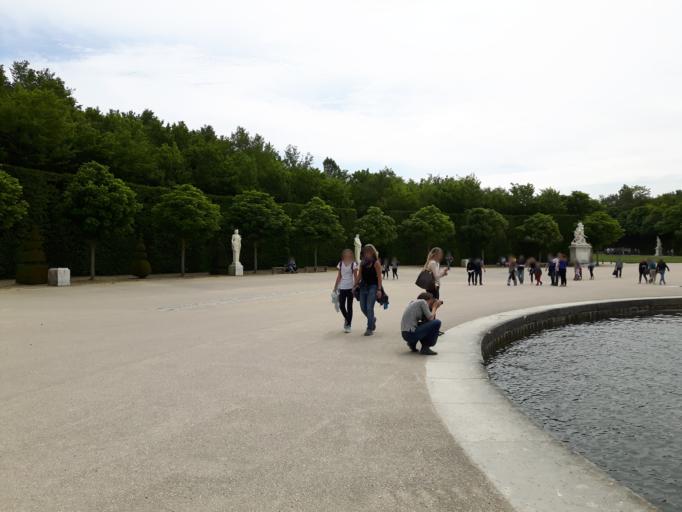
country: FR
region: Ile-de-France
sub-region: Departement des Yvelines
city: Le Chesnay
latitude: 48.8079
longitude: 2.1110
